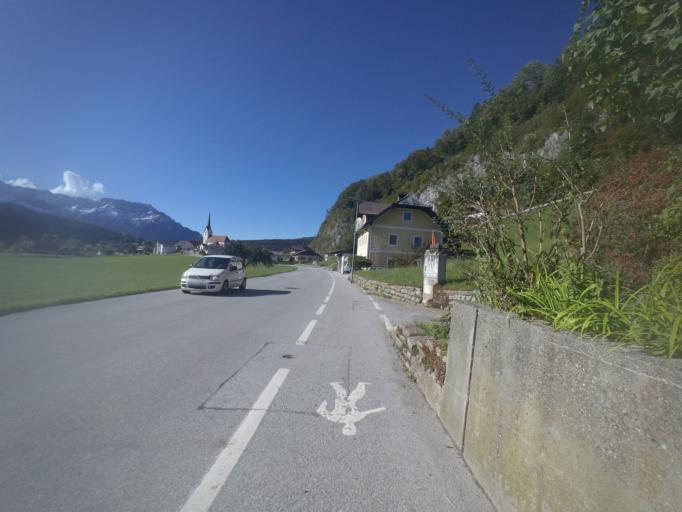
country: AT
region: Salzburg
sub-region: Politischer Bezirk Hallein
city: Adnet
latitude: 47.6946
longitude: 13.1368
